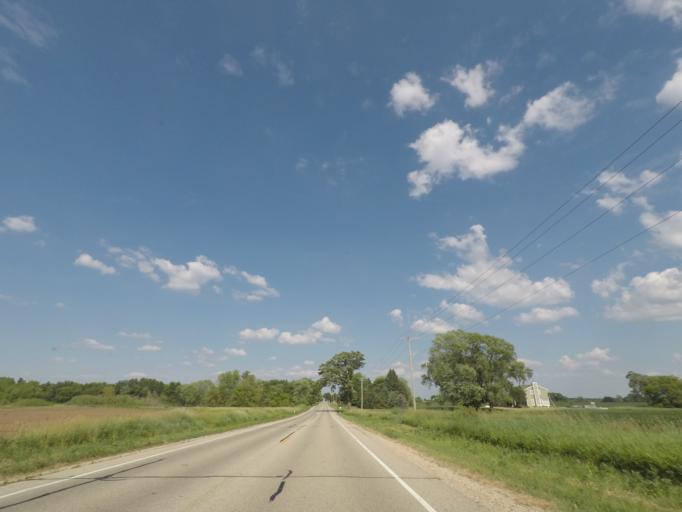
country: US
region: Wisconsin
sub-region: Walworth County
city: East Troy
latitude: 42.7930
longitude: -88.4815
